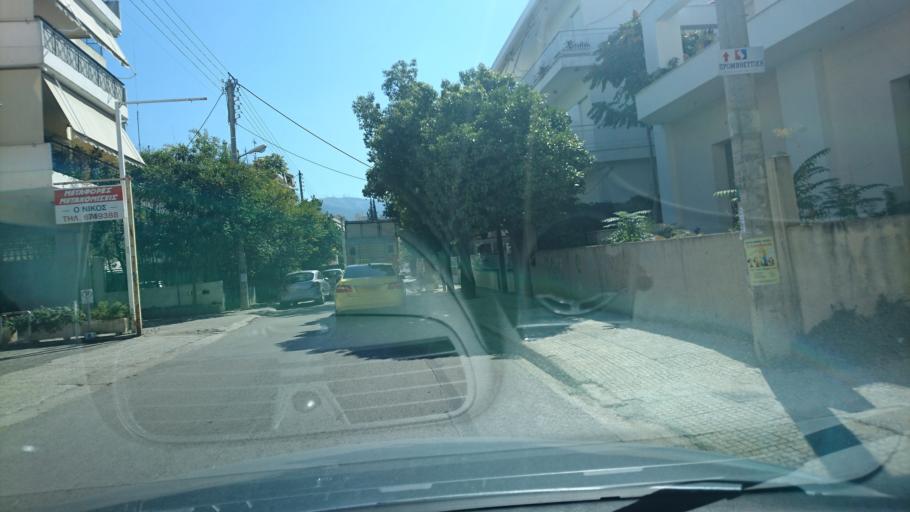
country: GR
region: Attica
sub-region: Nomarchia Athinas
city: Cholargos
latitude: 38.0110
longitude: 23.8006
